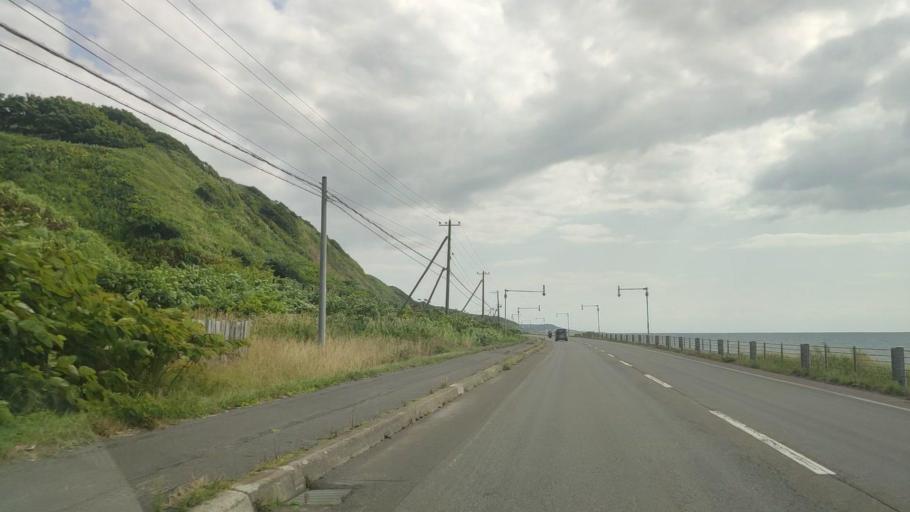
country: JP
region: Hokkaido
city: Rumoi
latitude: 44.1975
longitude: 141.6579
